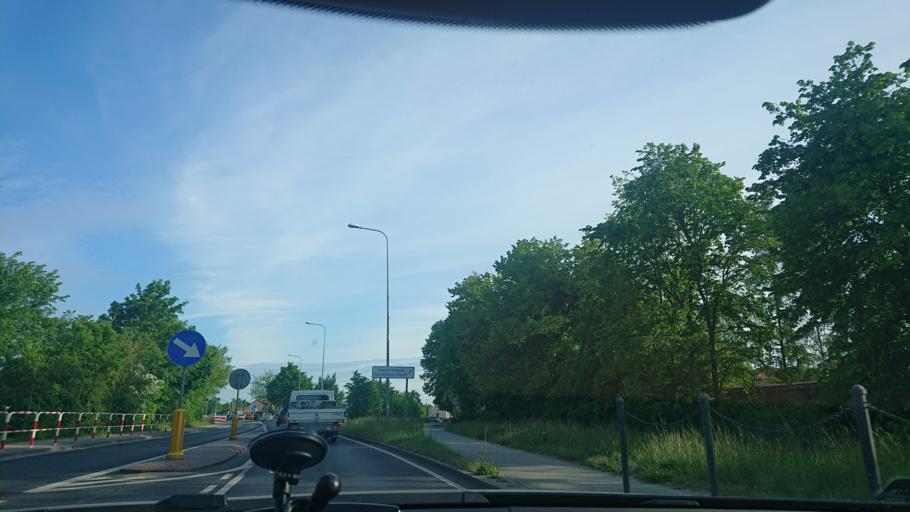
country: PL
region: Greater Poland Voivodeship
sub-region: Powiat gnieznienski
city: Gniezno
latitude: 52.5315
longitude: 17.5826
